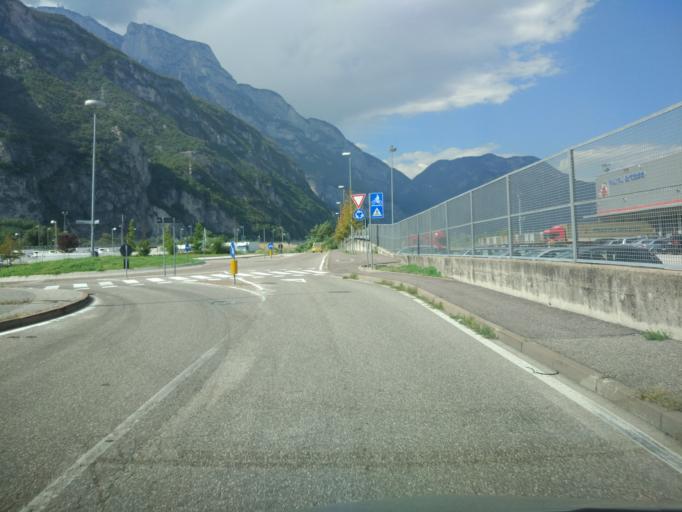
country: IT
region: Trentino-Alto Adige
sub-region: Provincia di Trento
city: Meano
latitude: 46.1136
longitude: 11.0908
